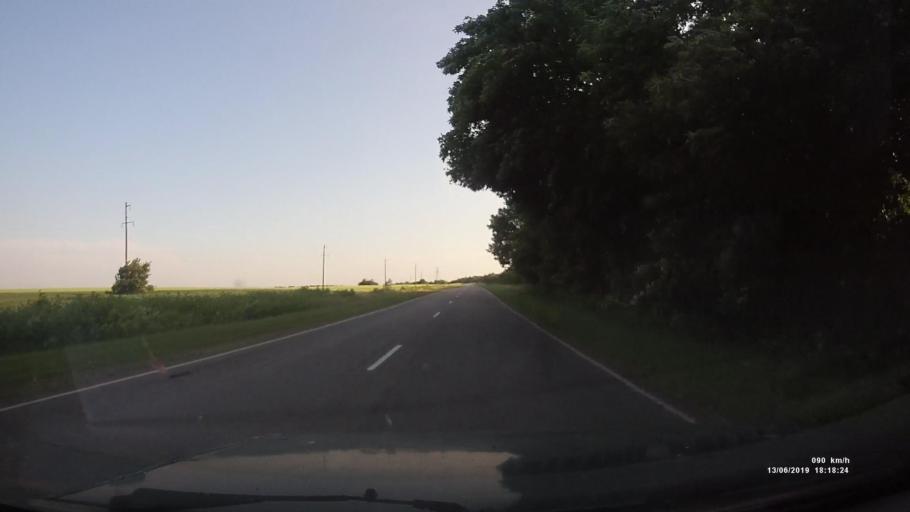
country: RU
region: Rostov
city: Kazanskaya
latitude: 49.9085
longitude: 41.3145
